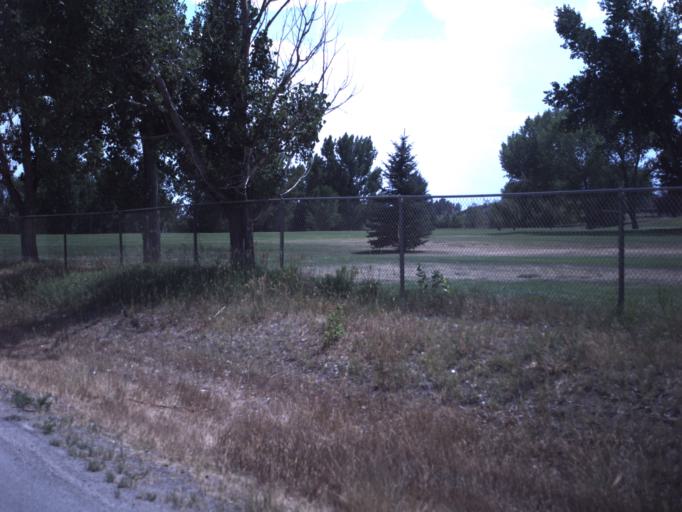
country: US
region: Utah
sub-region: Duchesne County
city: Roosevelt
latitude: 40.3069
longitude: -110.0051
